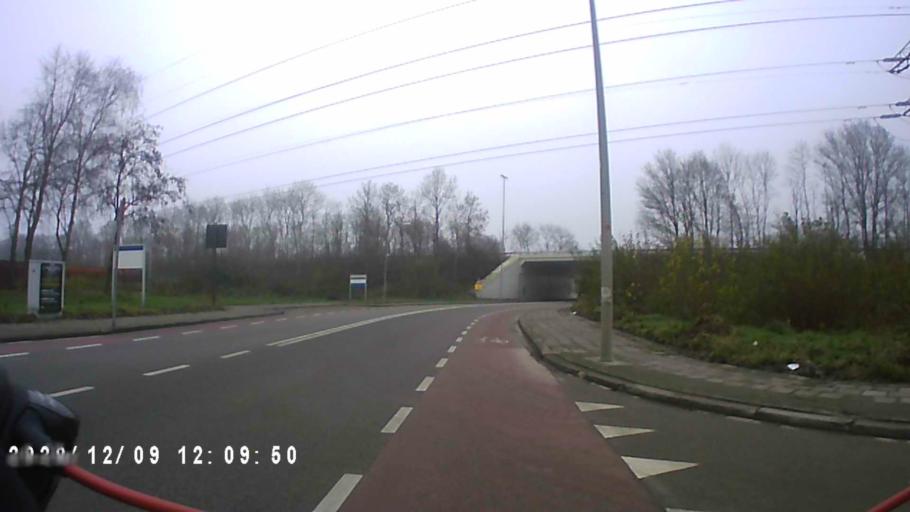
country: NL
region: Groningen
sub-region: Gemeente Groningen
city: Oosterpark
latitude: 53.2026
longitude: 6.6010
